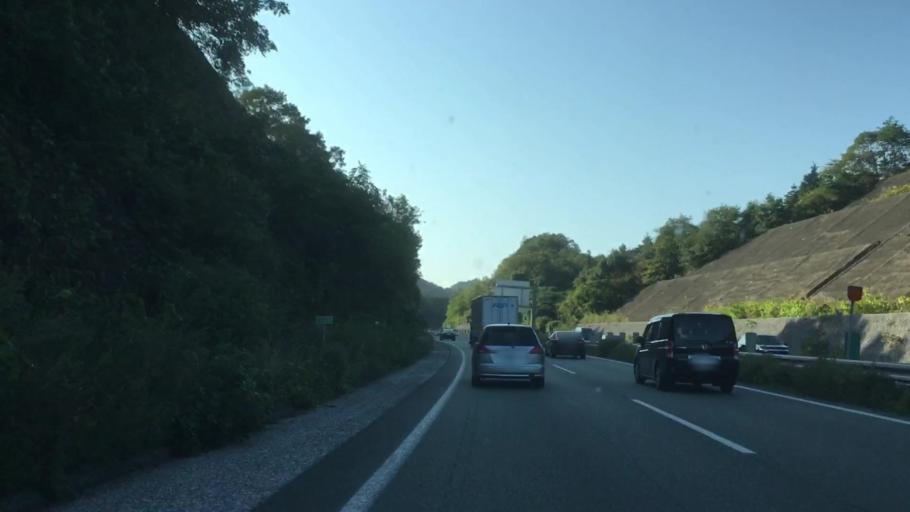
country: JP
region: Yamaguchi
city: Ogori-shimogo
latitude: 34.1281
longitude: 131.3817
